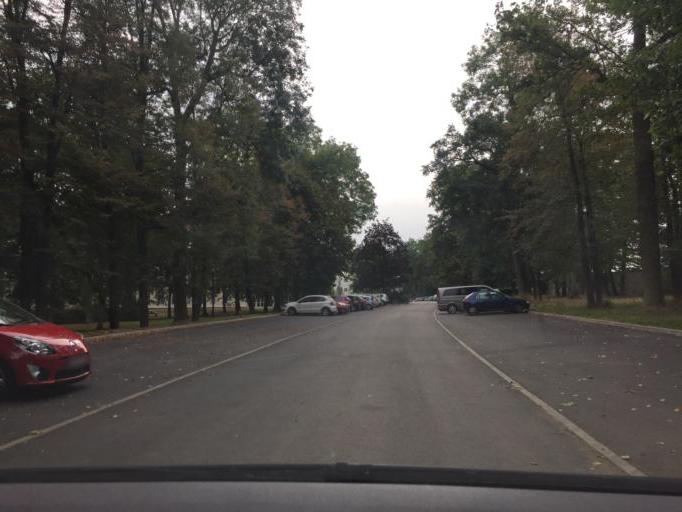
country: FR
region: Ile-de-France
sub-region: Departement des Yvelines
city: Jouy-en-Josas
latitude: 48.7564
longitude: 2.1616
